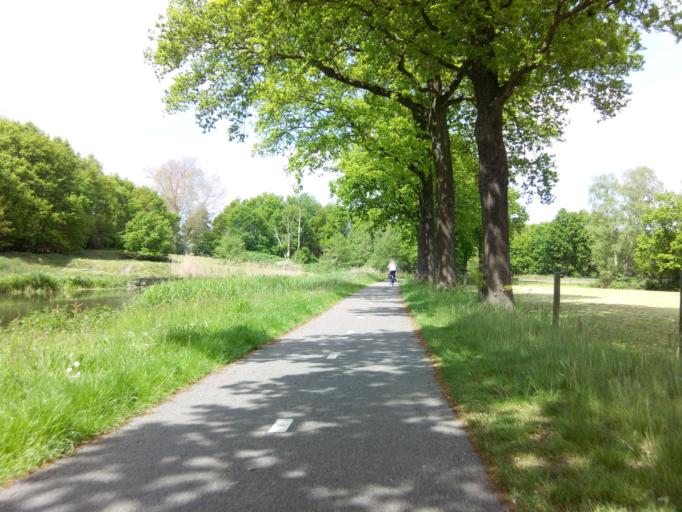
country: NL
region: Utrecht
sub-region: Gemeente Woudenberg
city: Woudenberg
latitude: 52.0842
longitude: 5.4527
